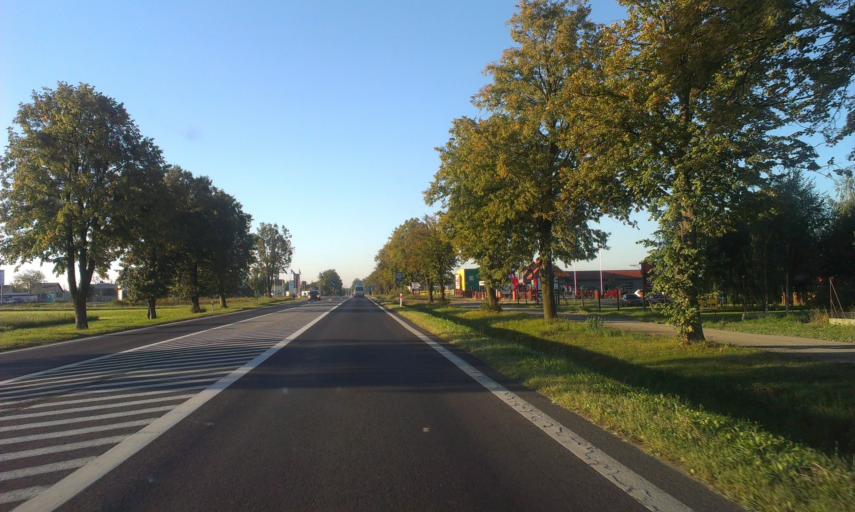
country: PL
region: Kujawsko-Pomorskie
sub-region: Powiat torunski
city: Lysomice
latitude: 53.0933
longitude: 18.6211
